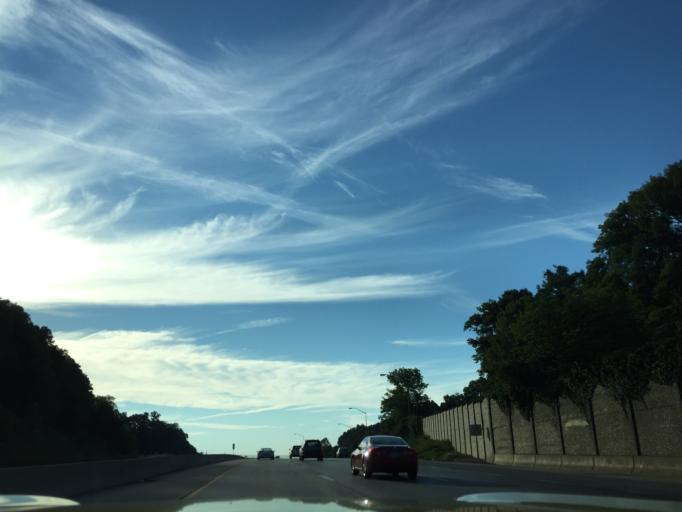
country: US
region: Pennsylvania
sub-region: Lehigh County
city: Emmaus
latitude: 40.5612
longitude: -75.4556
